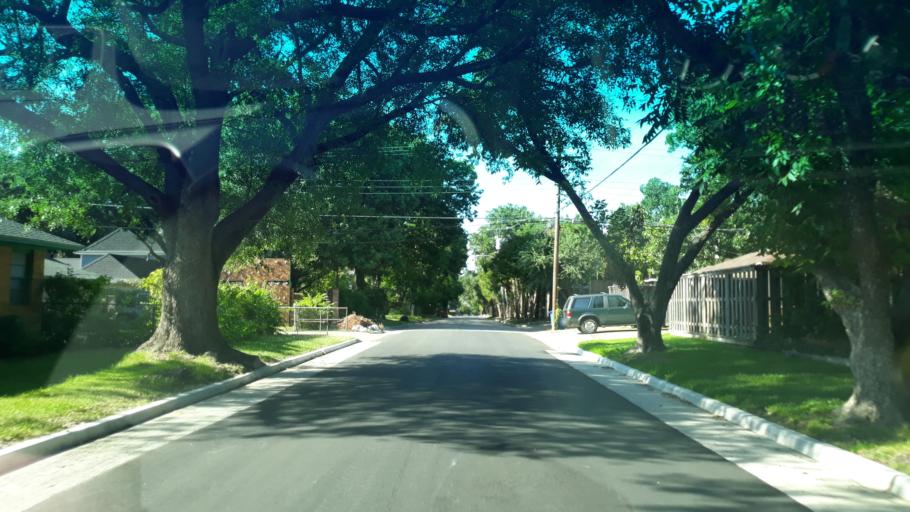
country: US
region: Texas
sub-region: Dallas County
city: Highland Park
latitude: 32.8267
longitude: -96.7560
